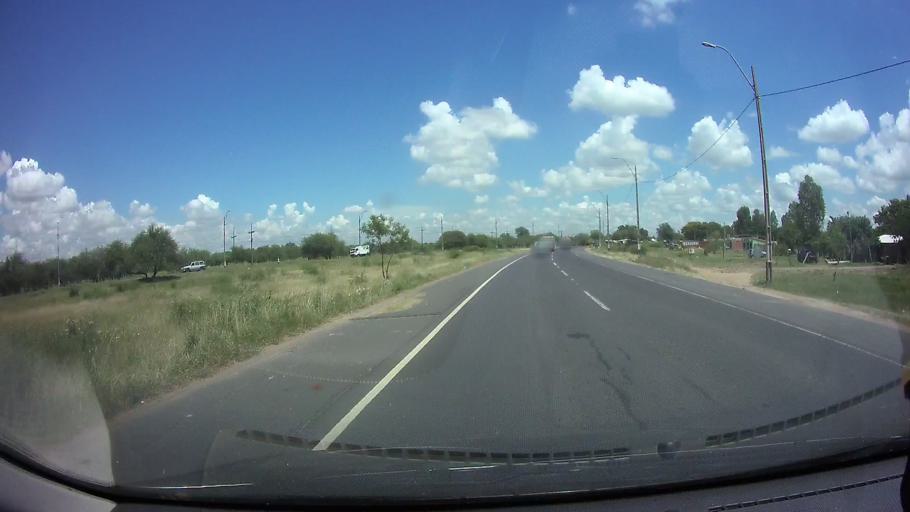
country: PY
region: Central
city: Colonia Mariano Roque Alonso
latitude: -25.1707
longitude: -57.5653
